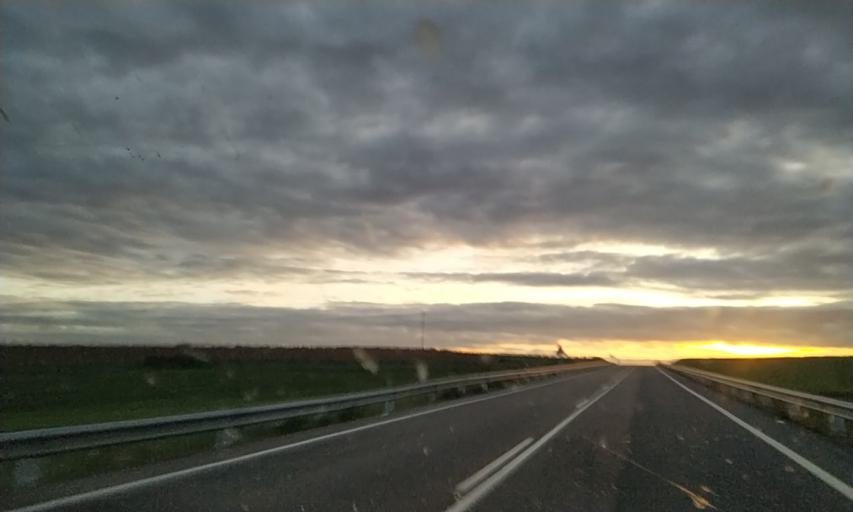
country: ES
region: Extremadura
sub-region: Provincia de Badajoz
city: La Roca de la Sierra
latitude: 39.0574
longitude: -6.7752
